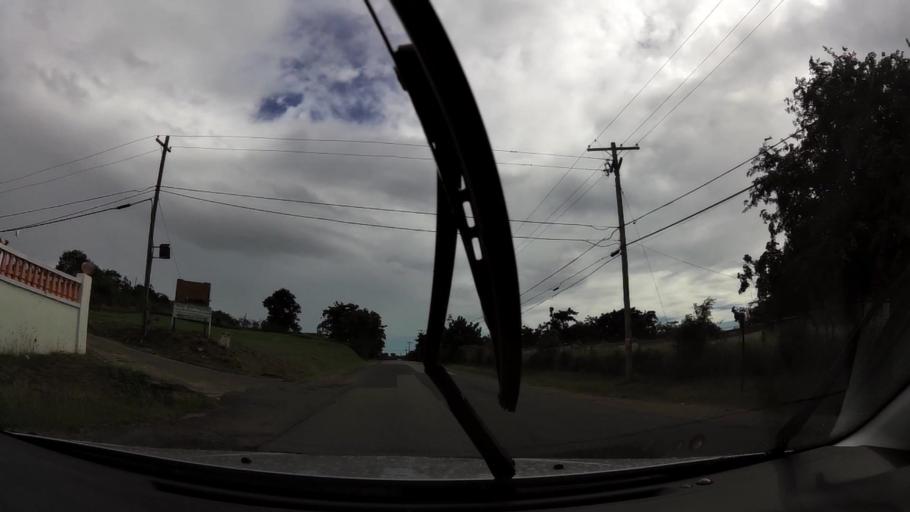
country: AG
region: Saint John
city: Saint John's
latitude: 17.1017
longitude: -61.8296
